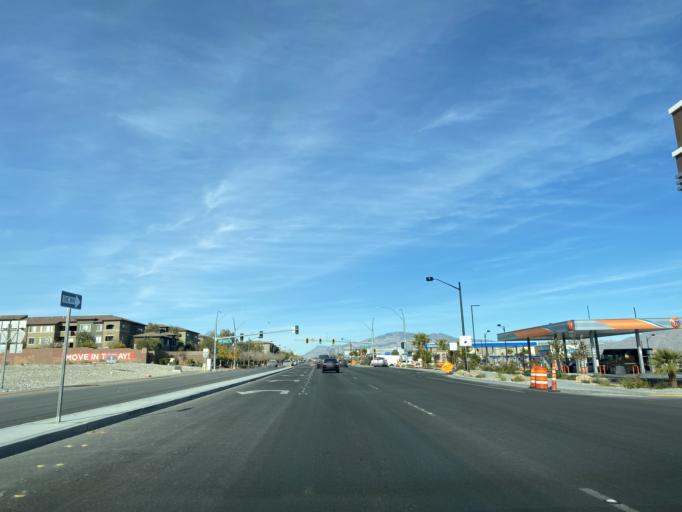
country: US
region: Nevada
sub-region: Clark County
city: Summerlin South
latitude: 36.2837
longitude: -115.3149
